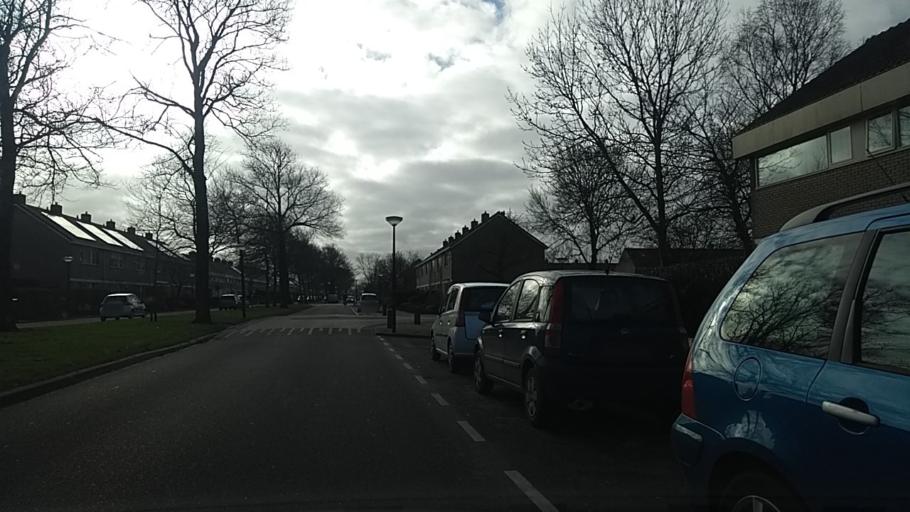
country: NL
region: Friesland
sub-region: Gemeente Harlingen
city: Harlingen
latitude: 53.1687
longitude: 5.4387
